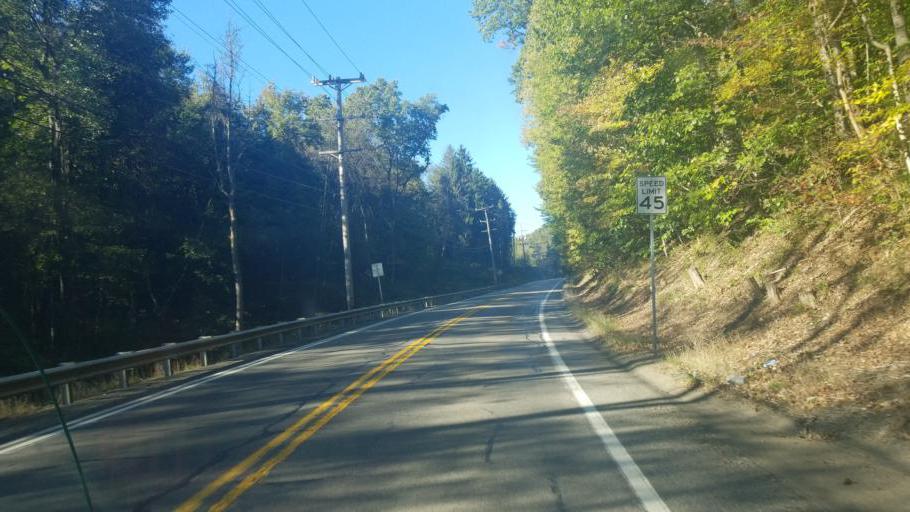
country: US
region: Pennsylvania
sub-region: Beaver County
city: Midland
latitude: 40.5470
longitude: -80.4204
